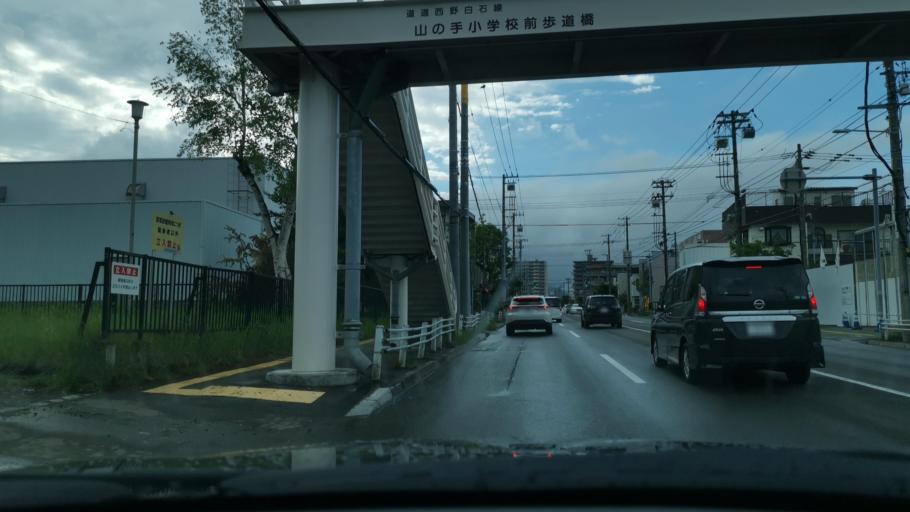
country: JP
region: Hokkaido
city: Sapporo
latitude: 43.0705
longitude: 141.2899
